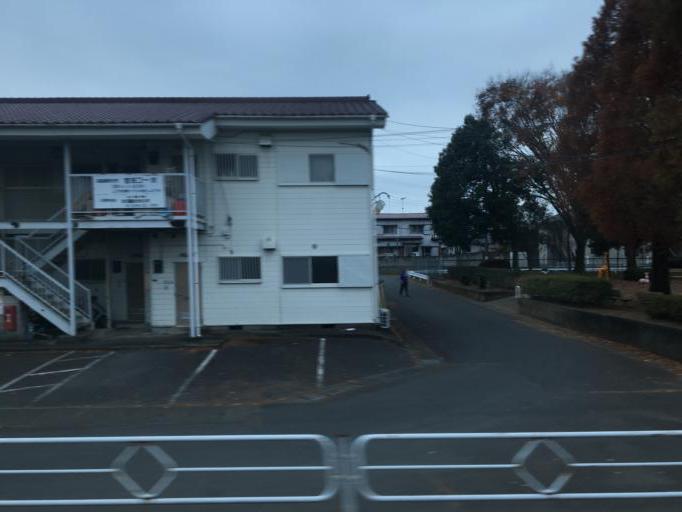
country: JP
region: Ibaraki
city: Yuki
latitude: 36.2995
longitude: 139.8625
